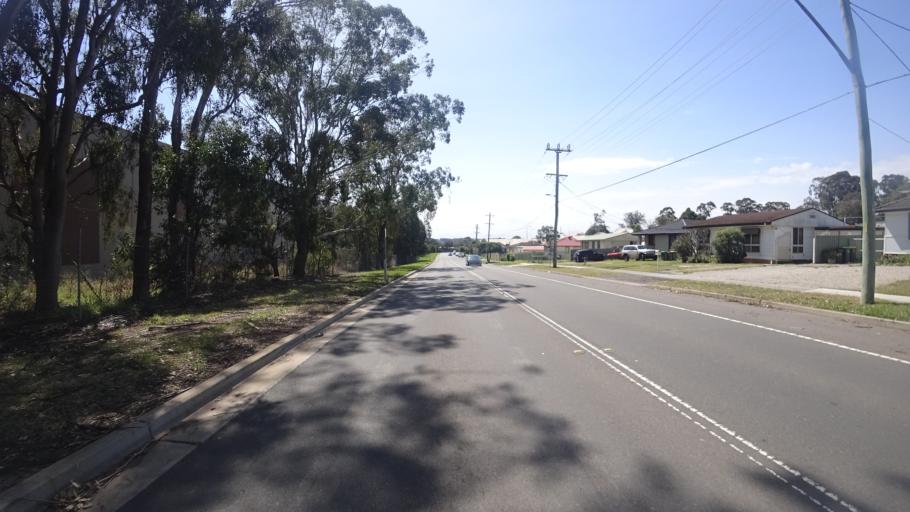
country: AU
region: New South Wales
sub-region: Liverpool
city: Miller
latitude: -33.9376
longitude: 150.8896
